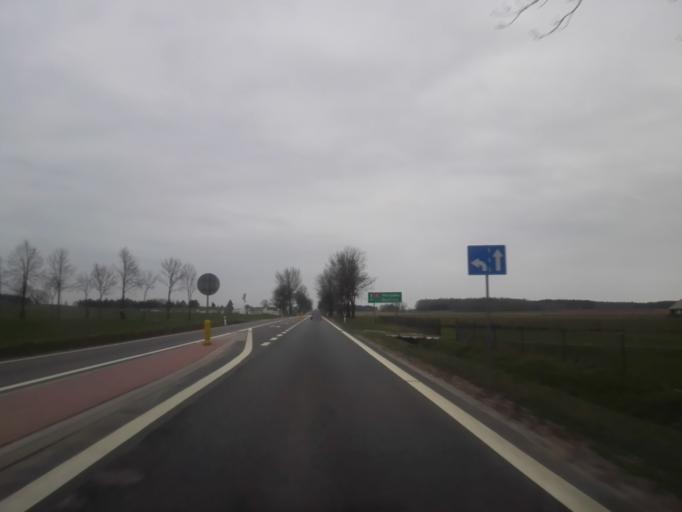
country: PL
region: Podlasie
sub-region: Powiat kolnenski
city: Stawiski
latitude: 53.4610
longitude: 22.1964
